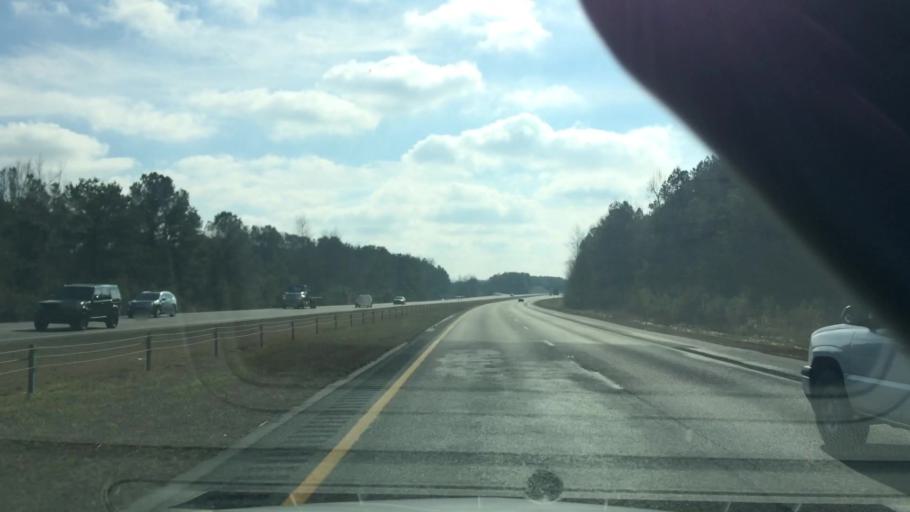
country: US
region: North Carolina
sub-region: Duplin County
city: Wallace
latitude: 34.6953
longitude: -77.9448
